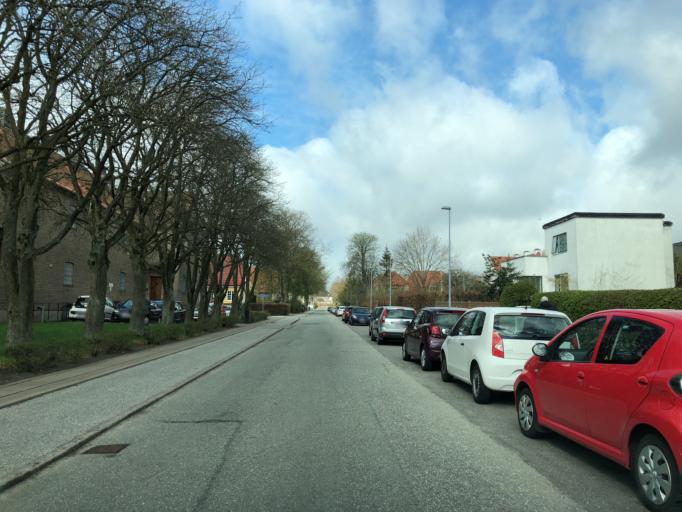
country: DK
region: North Denmark
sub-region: Alborg Kommune
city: Aalborg
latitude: 57.0470
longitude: 9.9075
